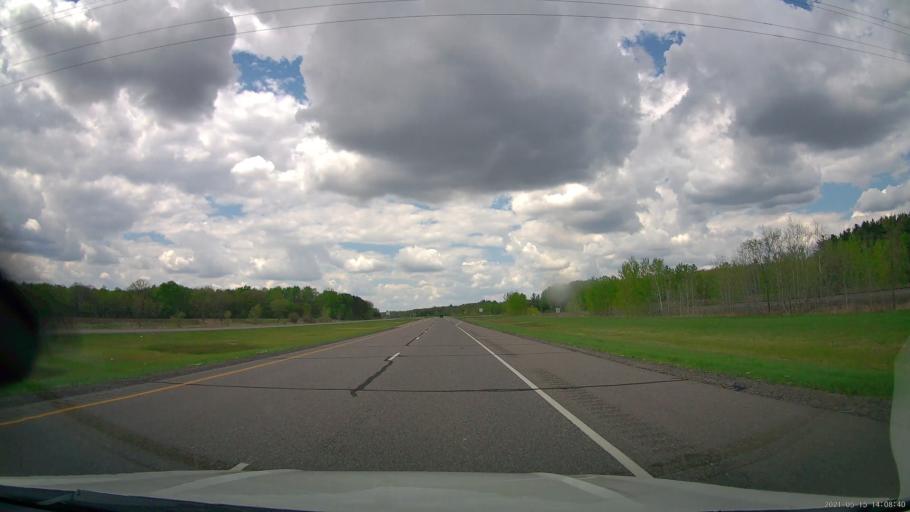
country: US
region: Minnesota
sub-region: Morrison County
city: Little Falls
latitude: 46.1172
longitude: -94.5383
